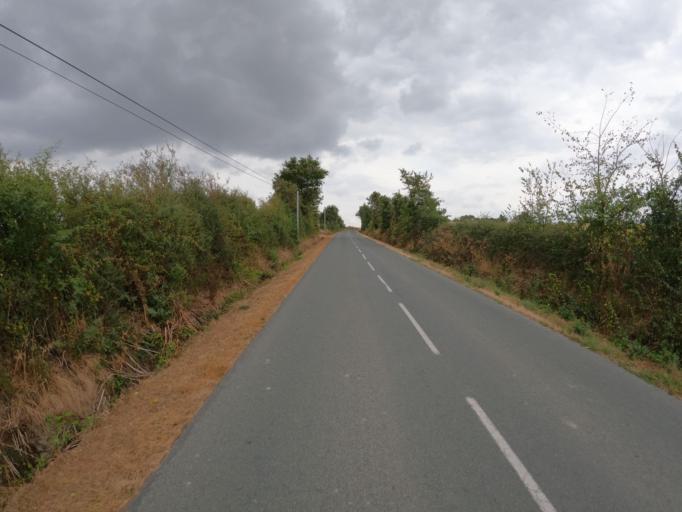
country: FR
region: Pays de la Loire
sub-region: Departement de la Vendee
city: Tiffauges
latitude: 46.9944
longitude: -1.0904
